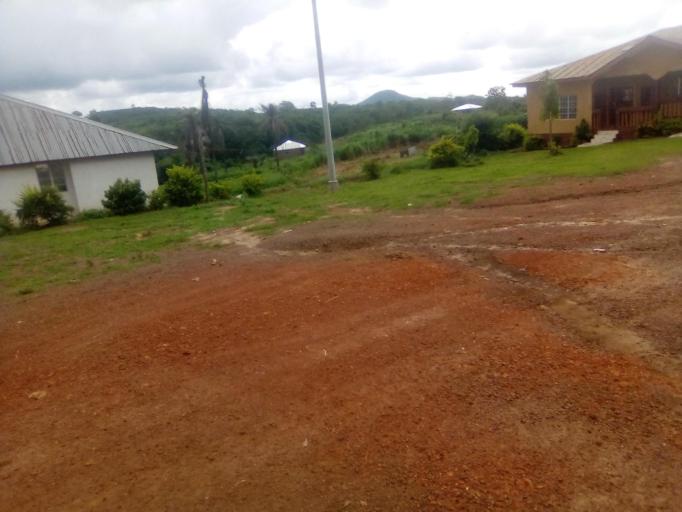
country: SL
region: Southern Province
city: Moyamba
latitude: 8.1443
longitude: -12.4371
